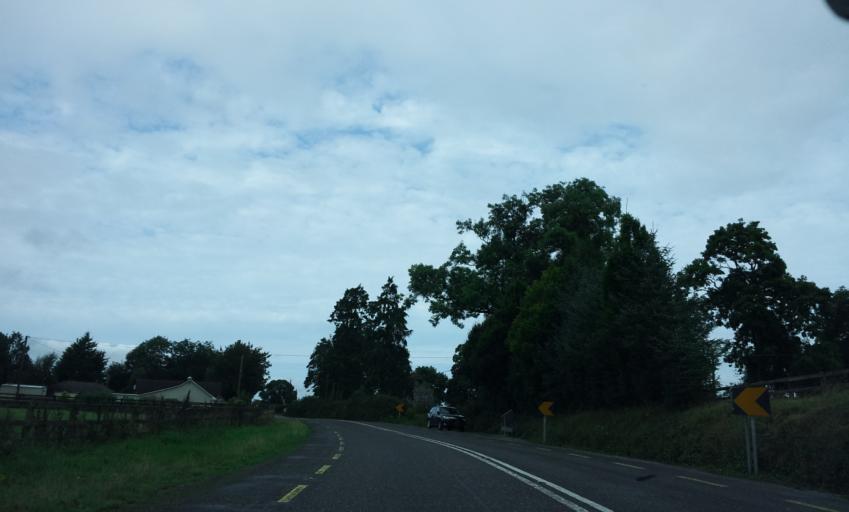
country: IE
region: Munster
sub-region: Ciarrai
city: Cill Airne
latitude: 52.0719
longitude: -9.5973
